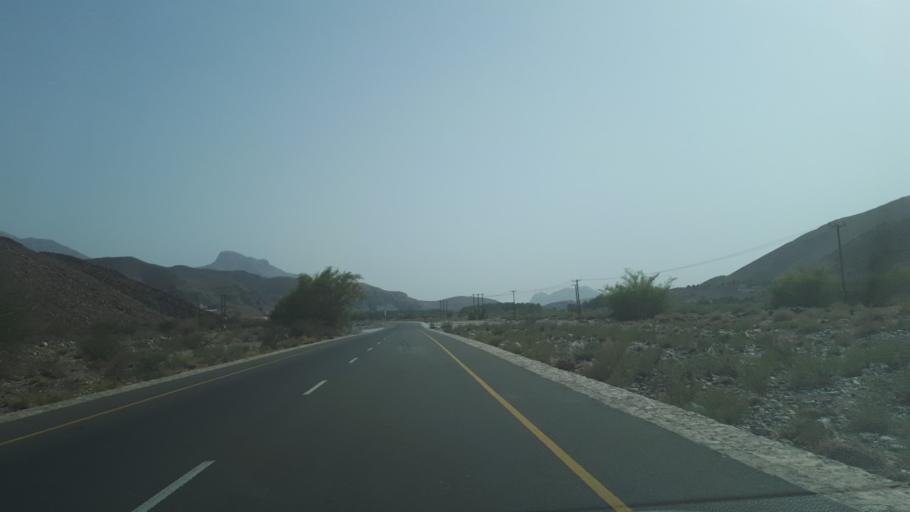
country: OM
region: Muhafazat ad Dakhiliyah
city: Bahla'
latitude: 23.2191
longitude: 56.9706
